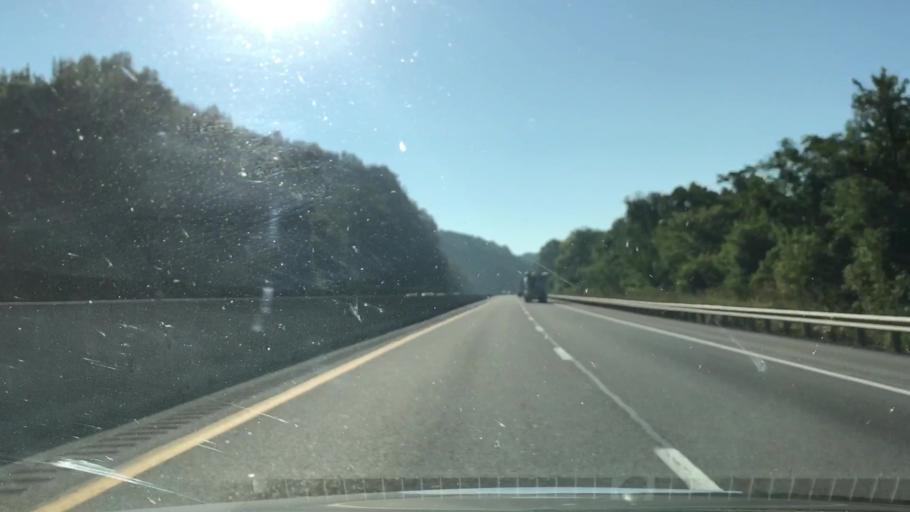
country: US
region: Tennessee
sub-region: Putnam County
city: Lafayette
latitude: 36.1044
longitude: -85.7566
